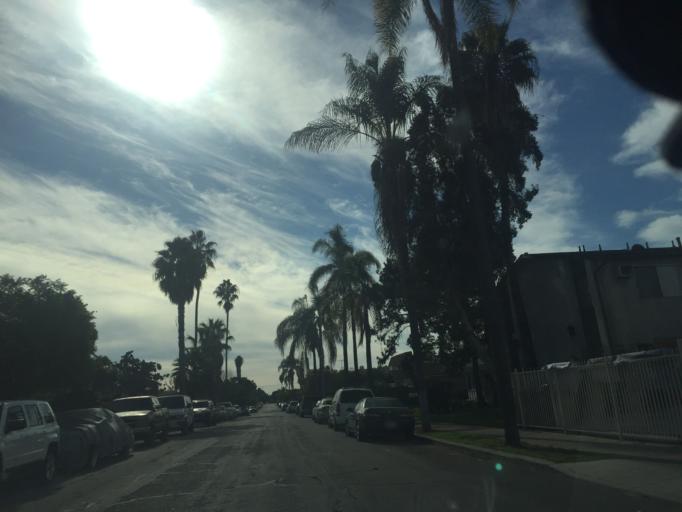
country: US
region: California
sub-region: San Diego County
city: Lemon Grove
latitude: 32.7527
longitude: -117.0955
